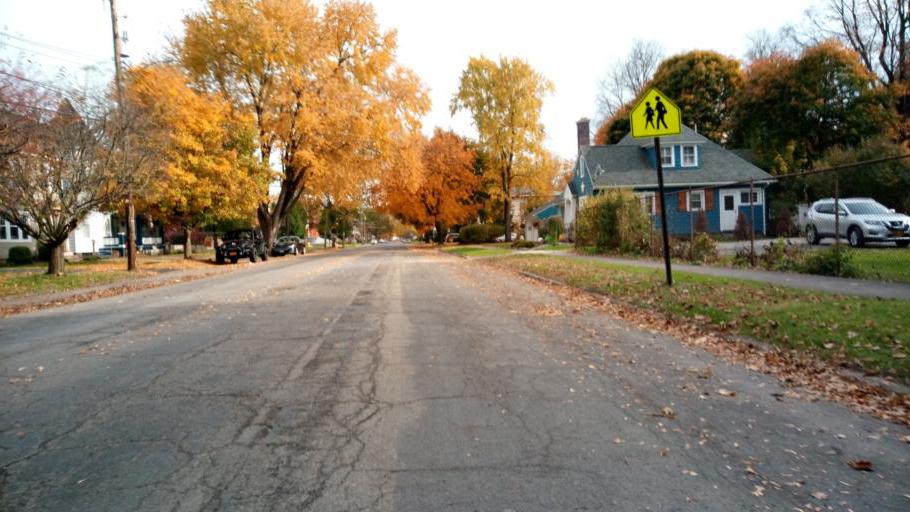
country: US
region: New York
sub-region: Chemung County
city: Elmira
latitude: 42.0853
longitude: -76.7958
